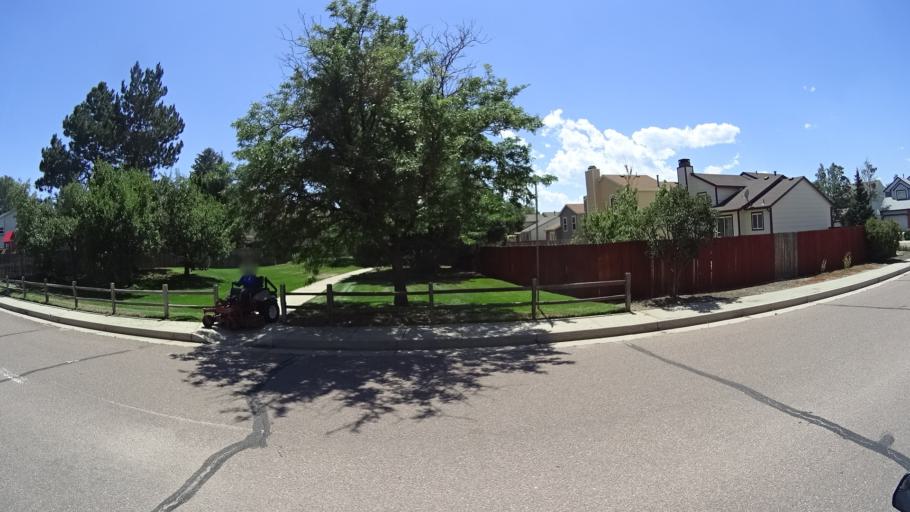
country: US
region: Colorado
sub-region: El Paso County
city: Black Forest
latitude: 38.9542
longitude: -104.7473
